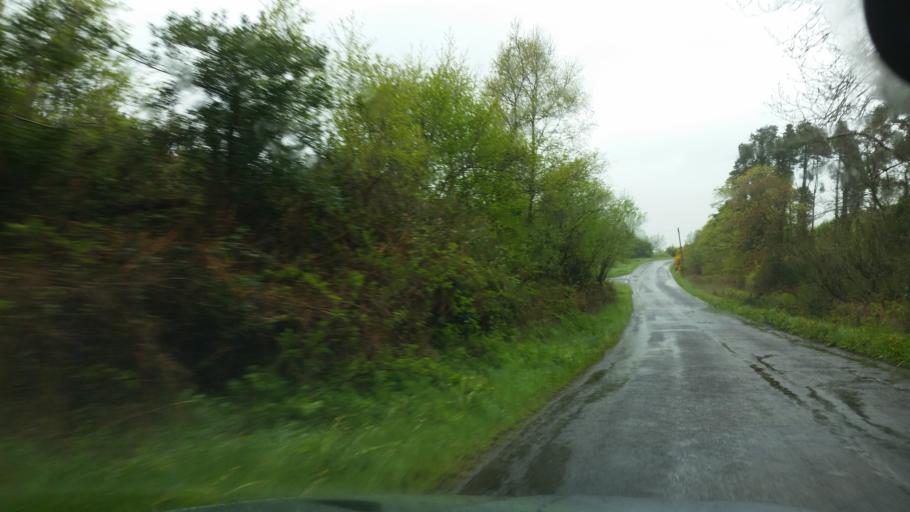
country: GB
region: Northern Ireland
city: Fivemiletown
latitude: 54.3550
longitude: -7.3022
